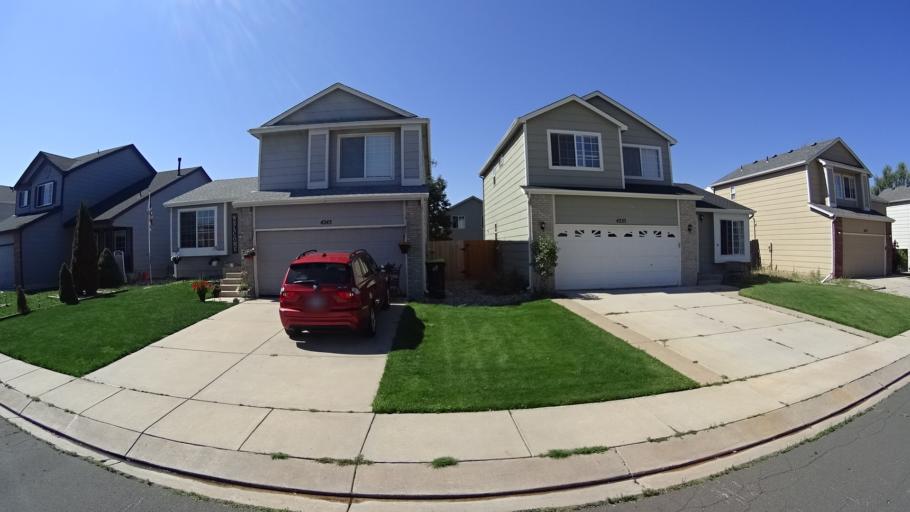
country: US
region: Colorado
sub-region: El Paso County
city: Black Forest
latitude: 38.9434
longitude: -104.7457
